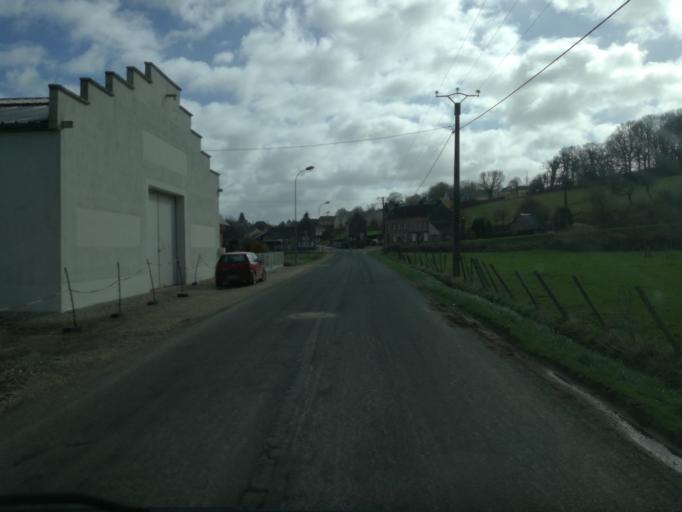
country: FR
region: Haute-Normandie
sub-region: Departement de la Seine-Maritime
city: Bretteville-du-Grand-Caux
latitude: 49.7047
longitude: 0.4425
